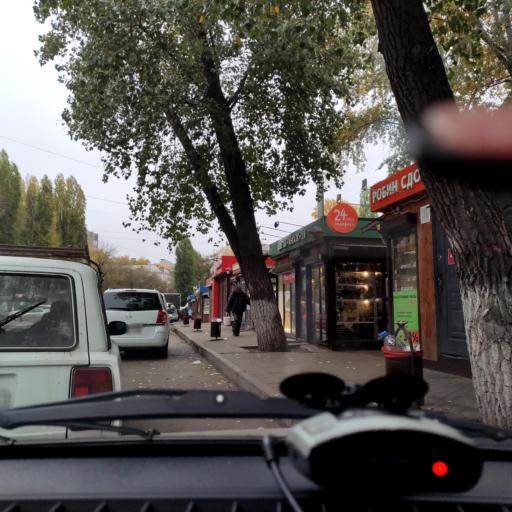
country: RU
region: Voronezj
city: Voronezh
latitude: 51.6841
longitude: 39.1955
